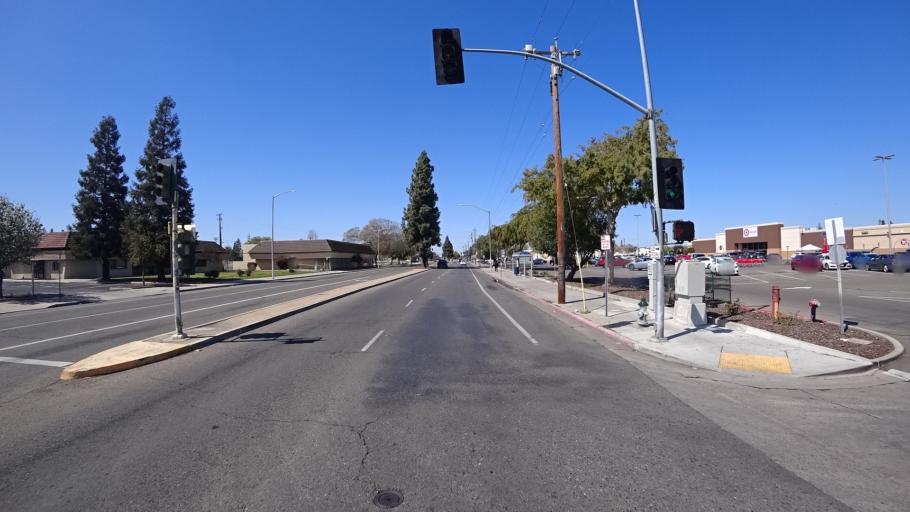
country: US
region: California
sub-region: Fresno County
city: Fresno
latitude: 36.7796
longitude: -119.7702
